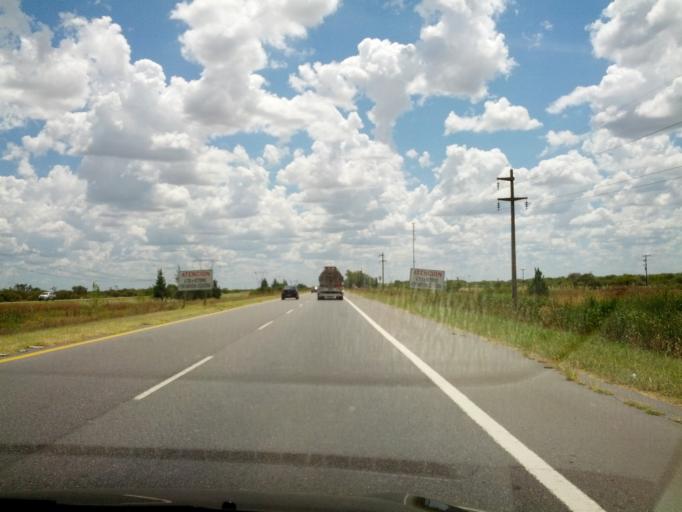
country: AR
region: Entre Rios
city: Ceibas
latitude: -33.4634
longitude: -58.8025
